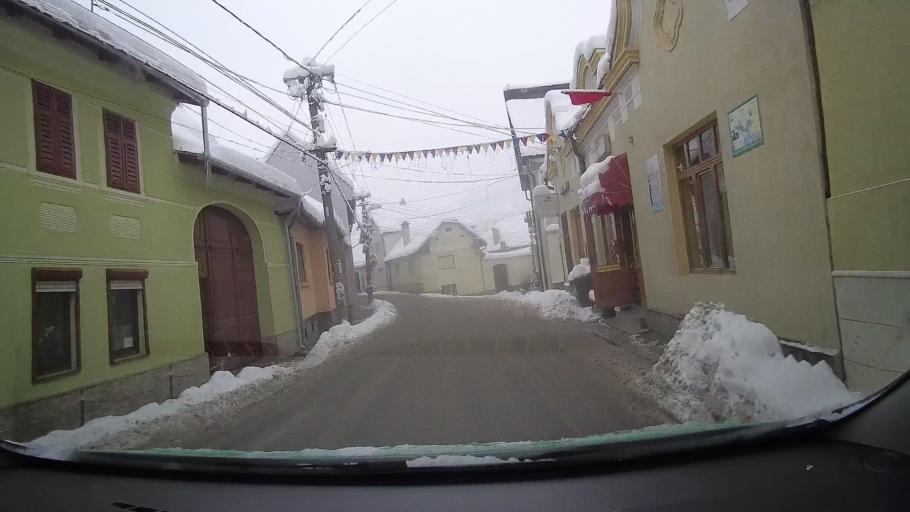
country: RO
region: Sibiu
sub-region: Comuna Tilisca
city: Tilisca
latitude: 45.7987
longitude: 23.8452
